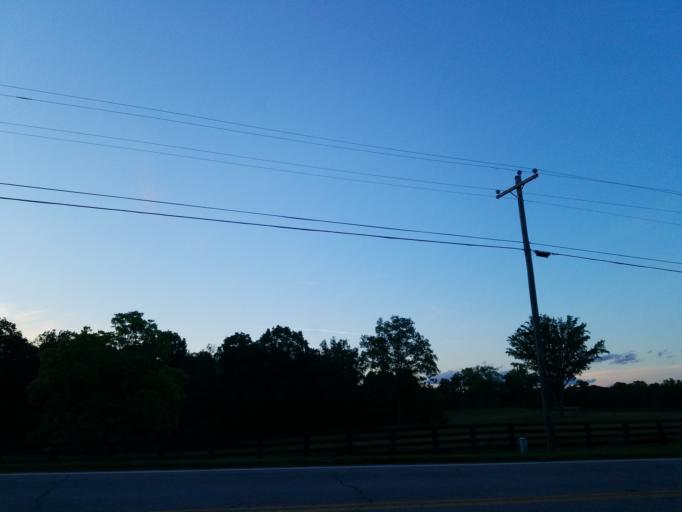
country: US
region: Georgia
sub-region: Lumpkin County
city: Dahlonega
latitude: 34.5619
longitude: -83.9074
